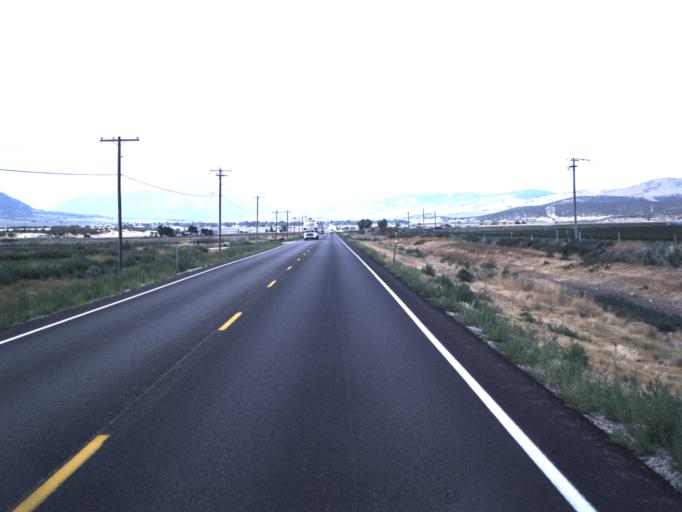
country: US
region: Utah
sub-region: Sanpete County
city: Fountain Green
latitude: 39.5894
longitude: -111.6163
